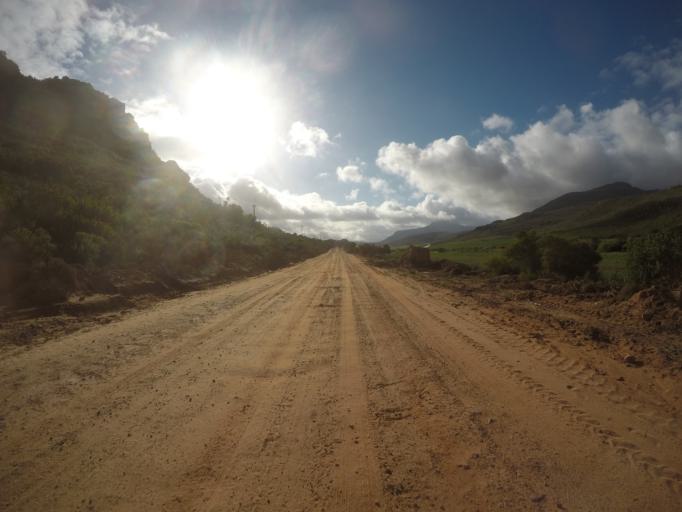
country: ZA
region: Western Cape
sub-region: West Coast District Municipality
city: Clanwilliam
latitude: -32.3433
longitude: 18.8146
